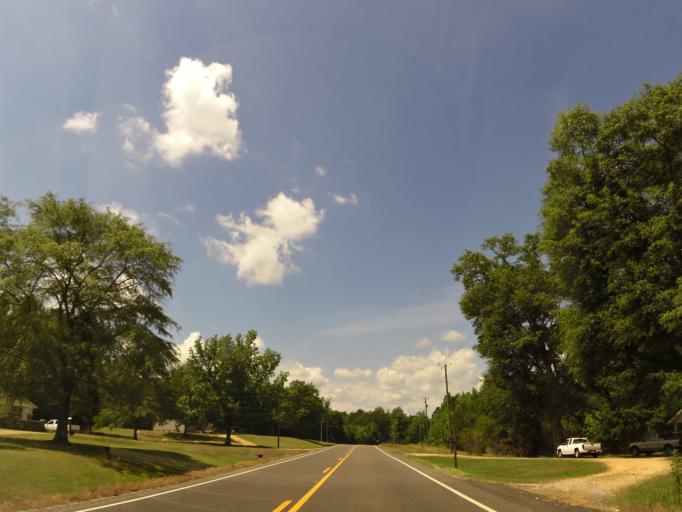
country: US
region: Alabama
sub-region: Lamar County
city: Sulligent
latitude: 33.9270
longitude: -88.0266
